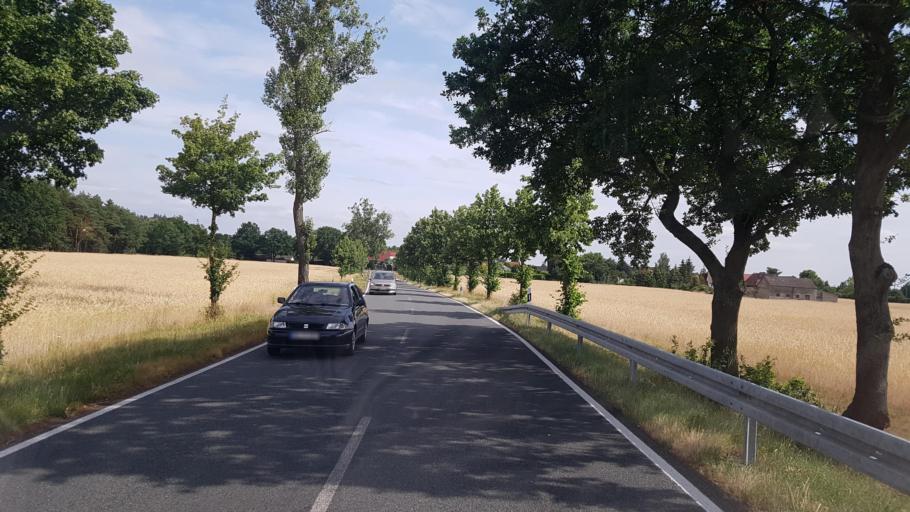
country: DE
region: Saxony-Anhalt
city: Muhlanger
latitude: 51.8754
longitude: 12.7487
